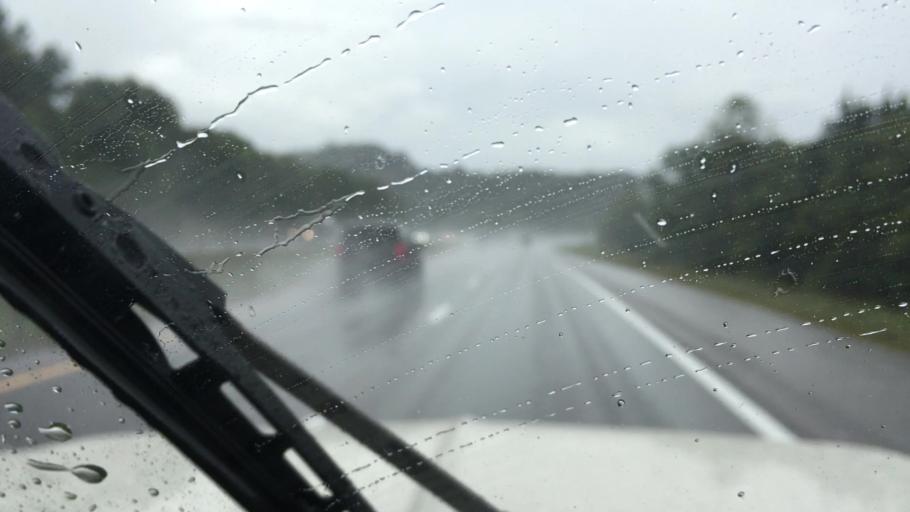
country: US
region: Tennessee
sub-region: Marshall County
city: Cornersville
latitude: 35.2358
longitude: -86.8877
